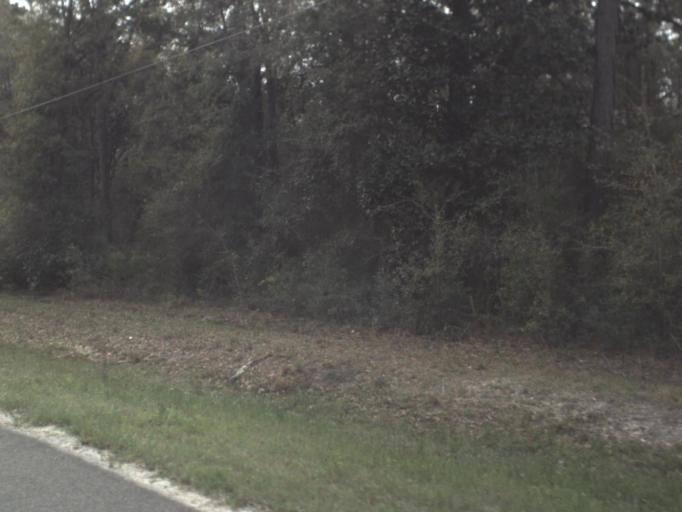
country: US
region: Florida
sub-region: Gulf County
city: Wewahitchka
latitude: 30.0655
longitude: -85.1919
